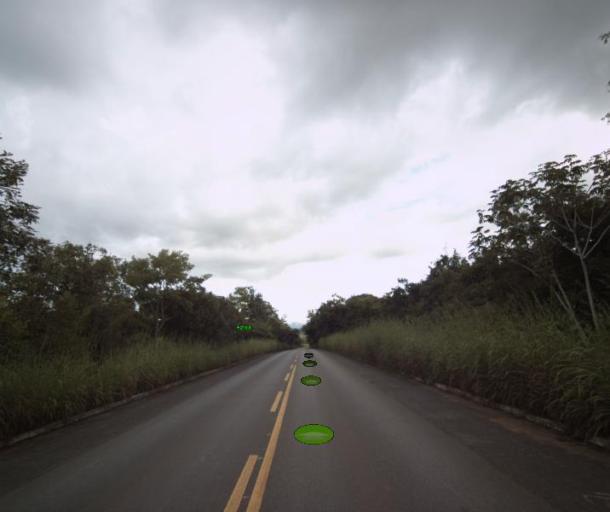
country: BR
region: Goias
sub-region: Niquelandia
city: Niquelandia
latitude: -14.5099
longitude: -48.5195
